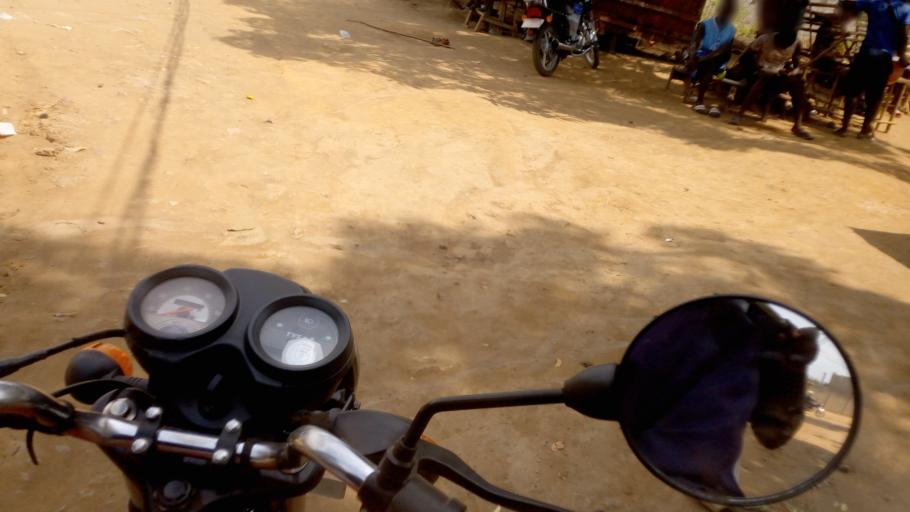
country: SL
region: Western Area
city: Waterloo
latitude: 8.3239
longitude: -13.0712
